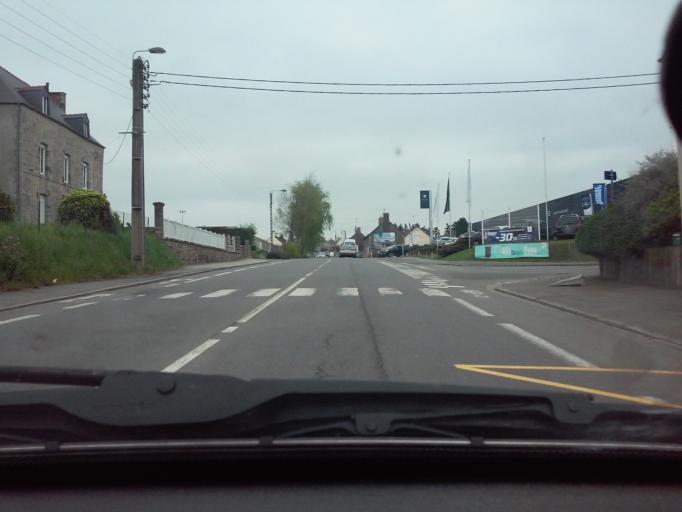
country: FR
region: Brittany
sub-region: Departement d'Ille-et-Vilaine
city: Fougeres
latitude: 48.3449
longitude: -1.1801
